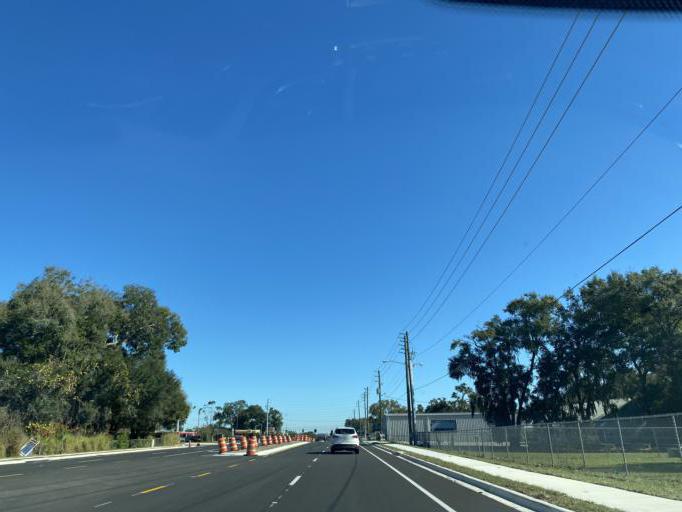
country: US
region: Florida
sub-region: Lake County
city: Fruitland Park
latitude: 28.8613
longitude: -81.9093
